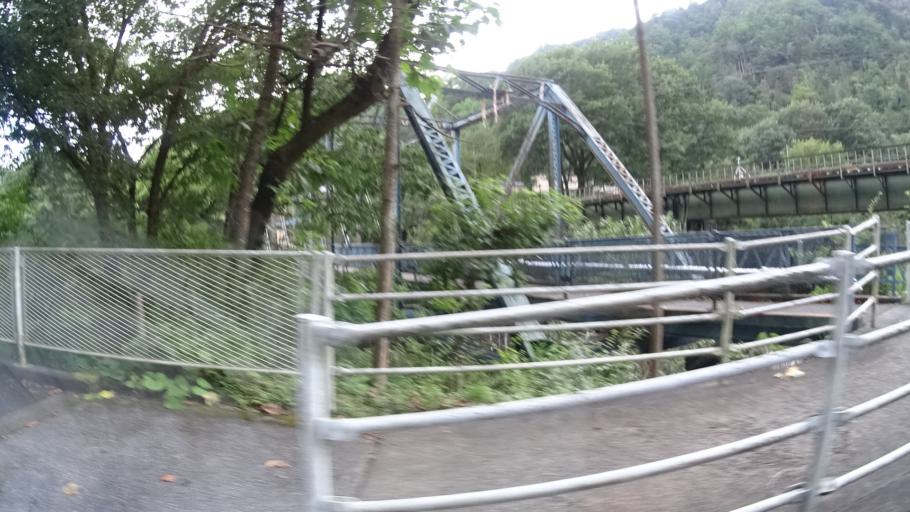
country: JP
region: Tochigi
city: Nikko
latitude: 36.6482
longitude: 139.4498
